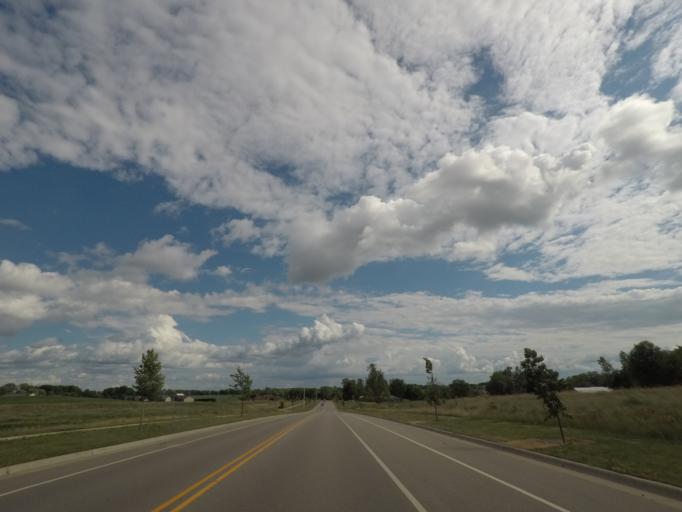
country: US
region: Wisconsin
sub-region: Rock County
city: Janesville
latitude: 42.6828
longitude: -89.0714
